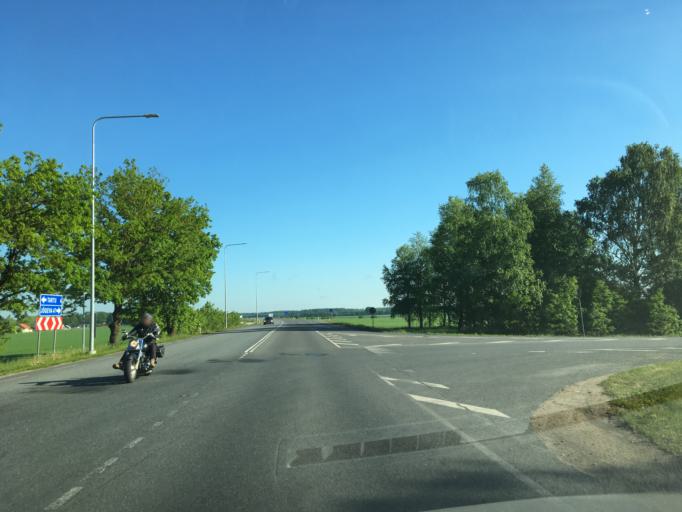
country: EE
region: Tartu
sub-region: Tartu linn
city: Tartu
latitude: 58.4098
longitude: 26.7080
